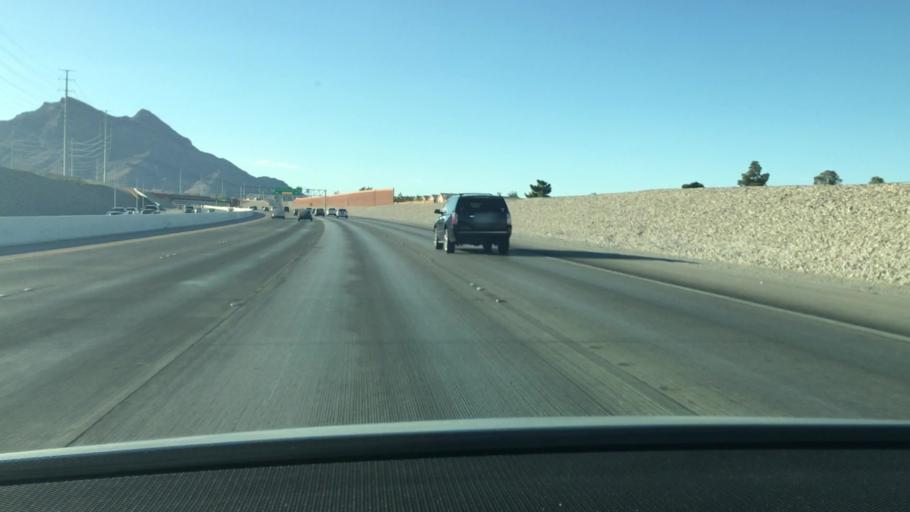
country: US
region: Nevada
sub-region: Clark County
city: Summerlin South
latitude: 36.1739
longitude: -115.3380
